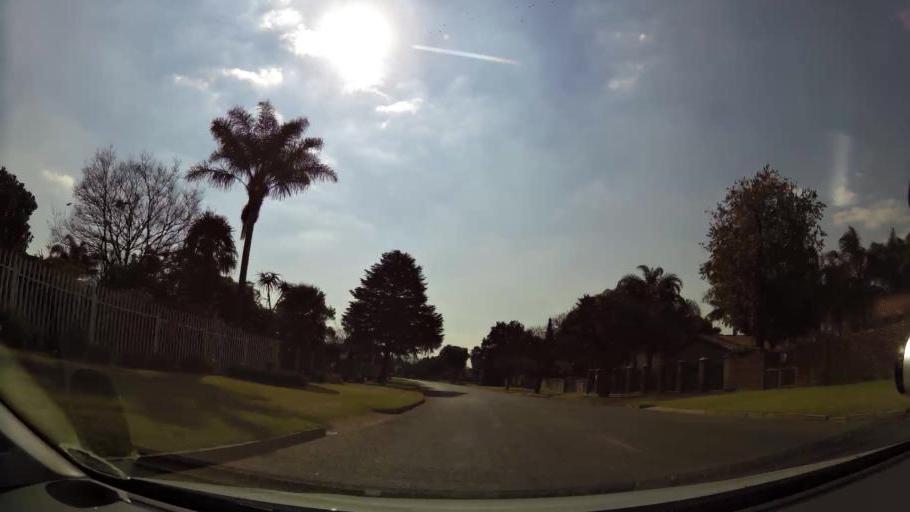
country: ZA
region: Gauteng
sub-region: City of Johannesburg Metropolitan Municipality
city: Modderfontein
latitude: -26.0864
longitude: 28.2342
